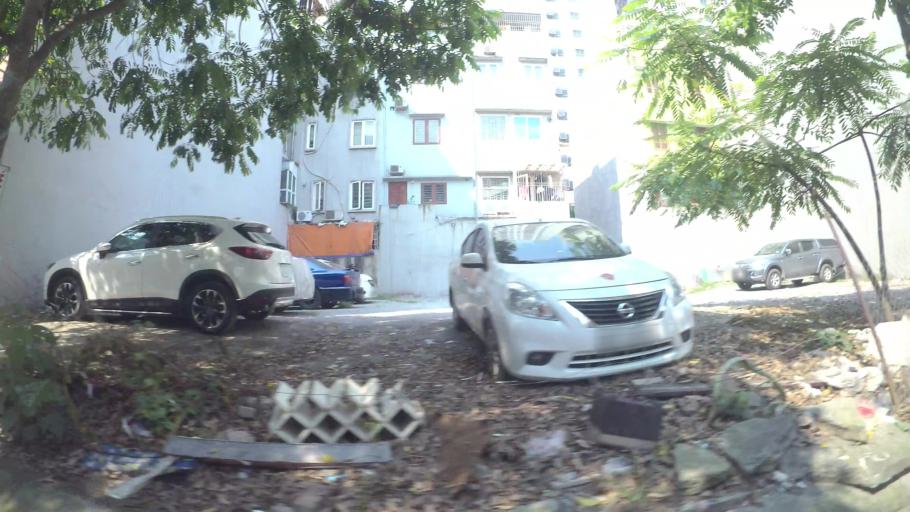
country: VN
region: Ha Noi
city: Ha Dong
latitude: 20.9556
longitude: 105.8080
